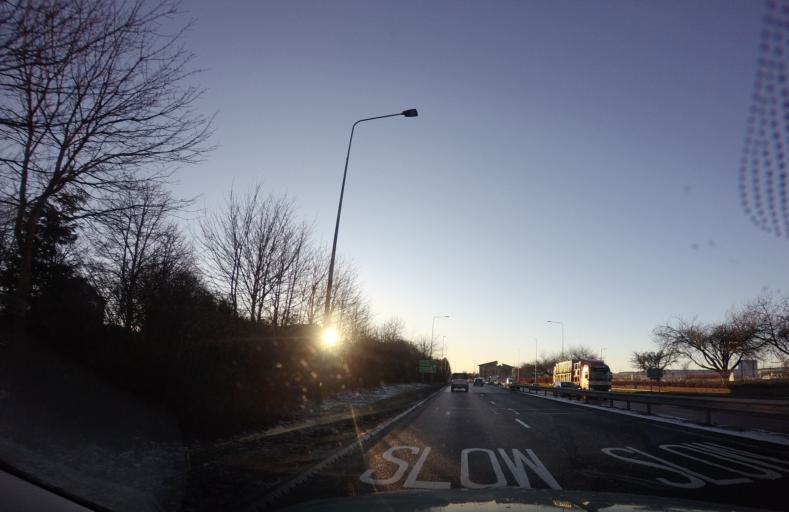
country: GB
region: Scotland
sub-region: Angus
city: Muirhead
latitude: 56.4744
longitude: -3.0469
